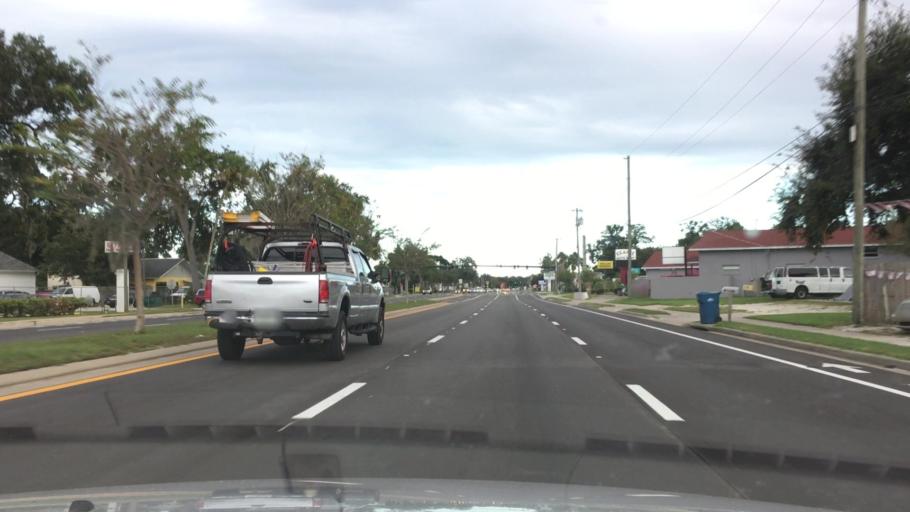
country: US
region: Florida
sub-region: Volusia County
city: Holly Hill
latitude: 29.2456
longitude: -81.0656
